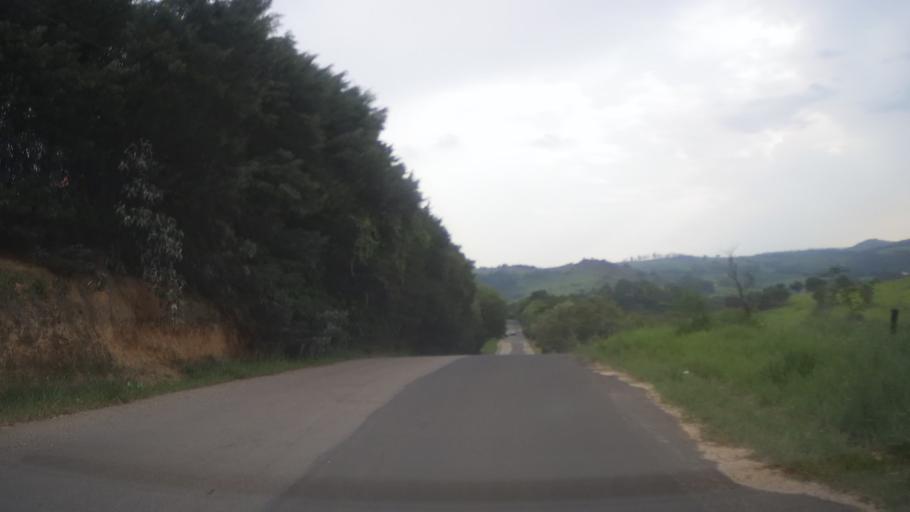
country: BR
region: Sao Paulo
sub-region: Itupeva
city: Itupeva
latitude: -23.1840
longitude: -47.0876
